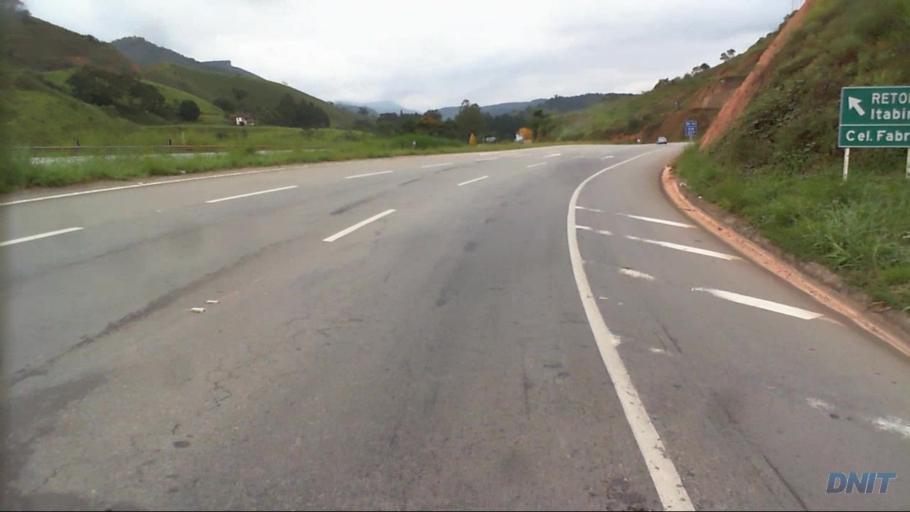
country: BR
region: Minas Gerais
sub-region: Nova Era
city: Nova Era
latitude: -19.7530
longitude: -43.0269
